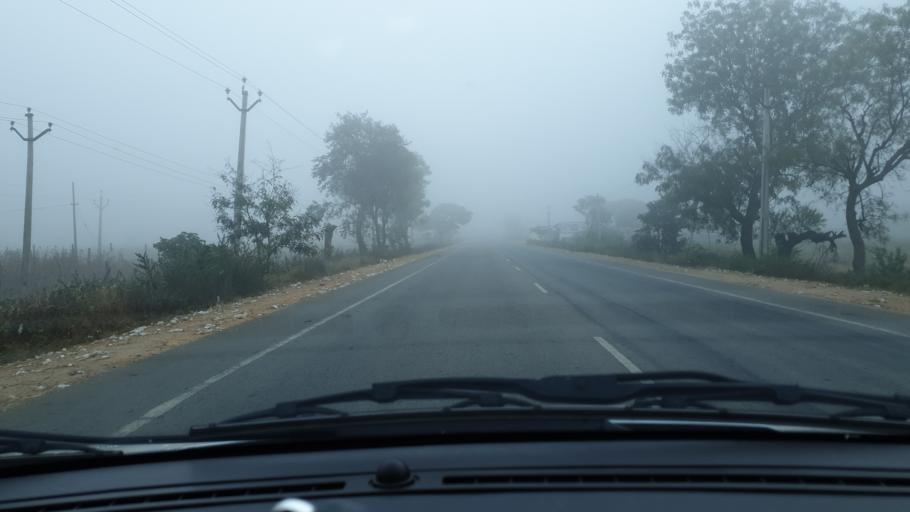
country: IN
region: Telangana
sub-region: Mahbubnagar
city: Nagar Karnul
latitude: 16.6644
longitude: 78.5608
